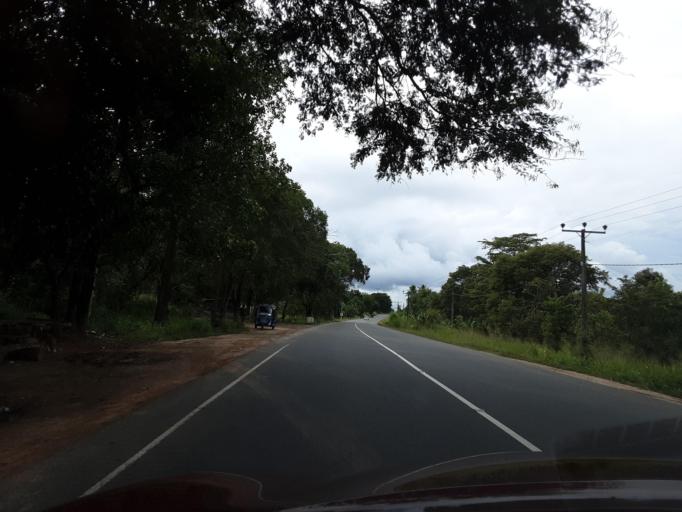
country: LK
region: Uva
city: Badulla
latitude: 7.3883
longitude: 81.1425
